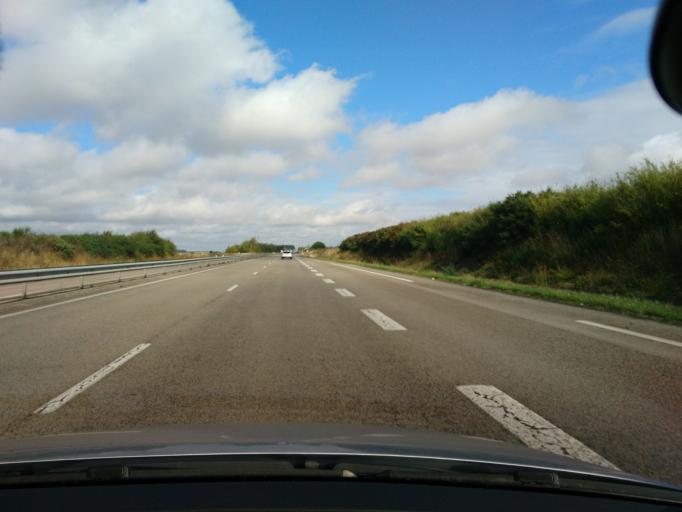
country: FR
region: Haute-Normandie
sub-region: Departement de l'Eure
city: Damville
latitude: 48.8921
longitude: 1.1720
